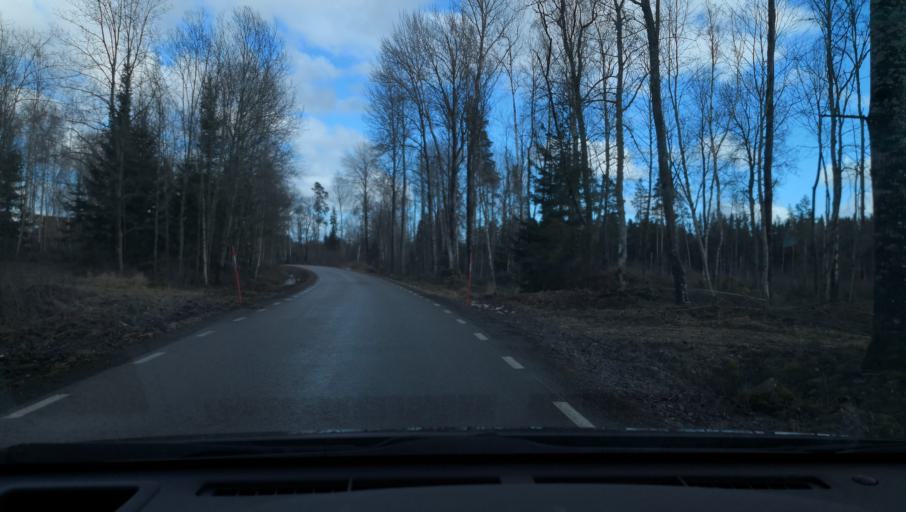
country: SE
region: OErebro
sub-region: Lindesbergs Kommun
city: Fellingsbro
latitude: 59.3394
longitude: 15.6930
